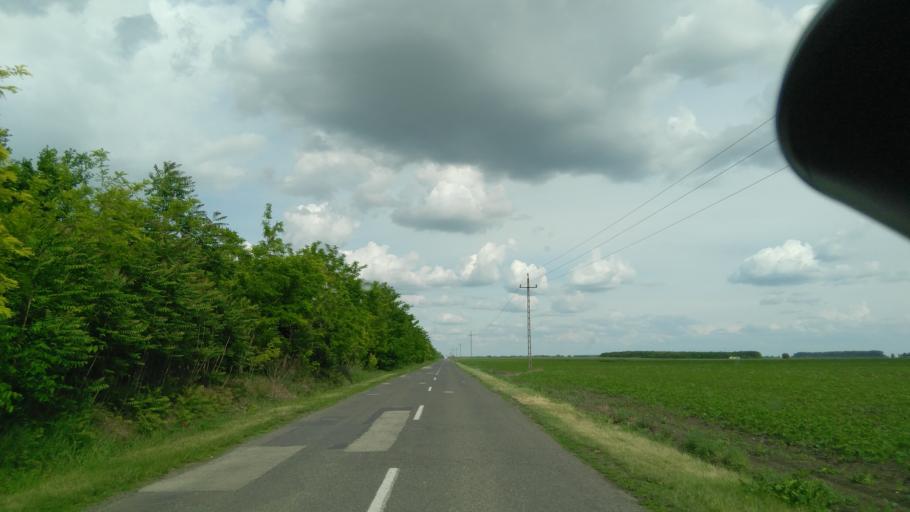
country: HU
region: Bekes
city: Mezohegyes
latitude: 46.3130
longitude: 20.8490
